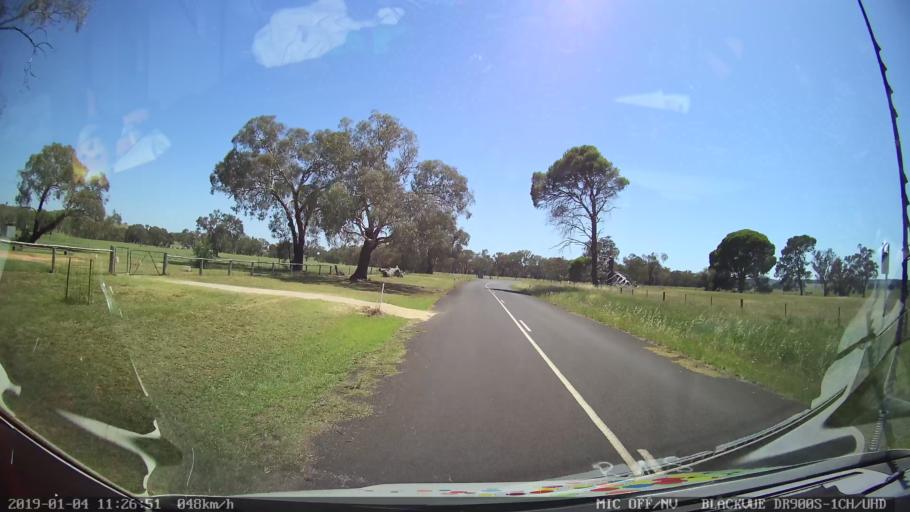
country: AU
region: New South Wales
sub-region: Cabonne
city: Molong
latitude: -33.1124
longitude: 148.7575
